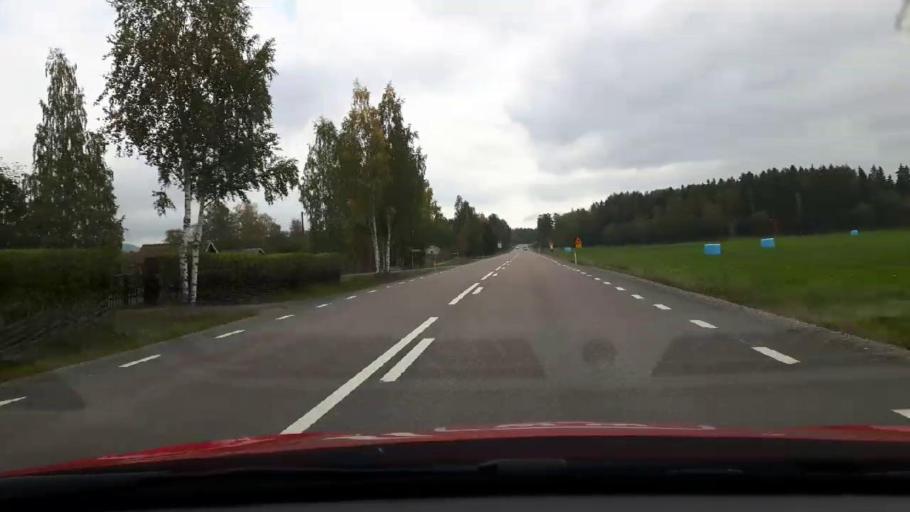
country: SE
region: Gaevleborg
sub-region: Bollnas Kommun
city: Bollnas
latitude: 61.3119
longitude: 16.4461
